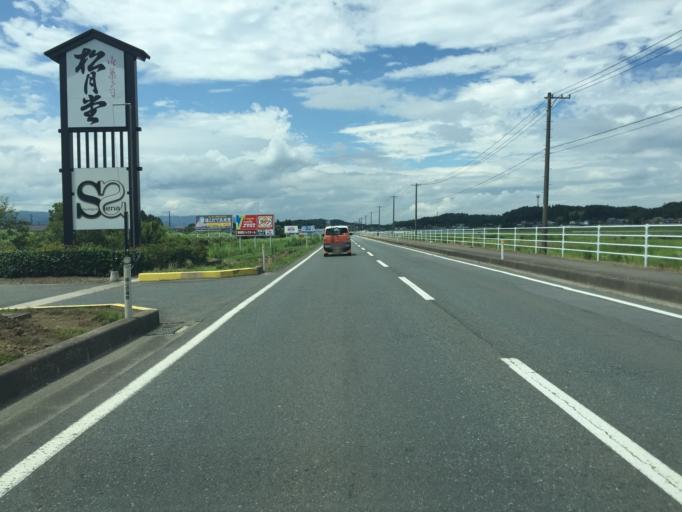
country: JP
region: Fukushima
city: Namie
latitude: 37.7097
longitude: 140.9652
